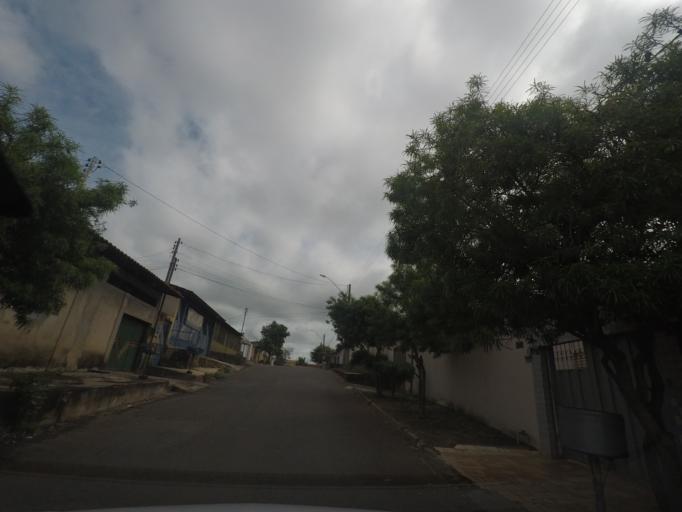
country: BR
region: Goias
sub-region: Goiania
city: Goiania
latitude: -16.6626
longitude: -49.1925
